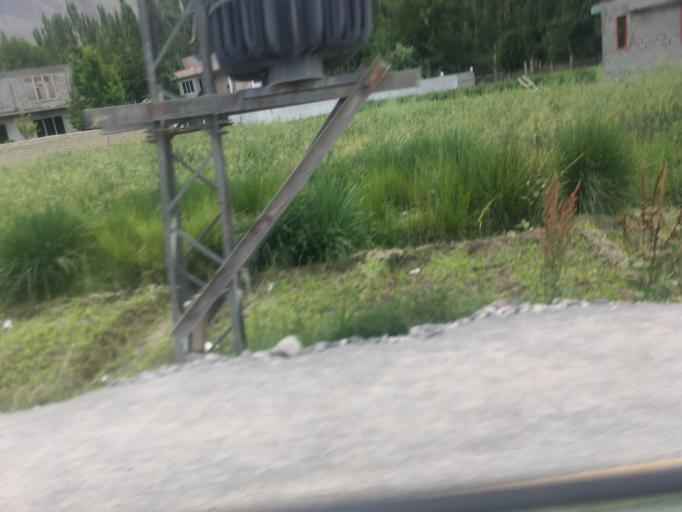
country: PK
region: Gilgit-Baltistan
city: Skardu
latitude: 35.2908
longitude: 75.6160
